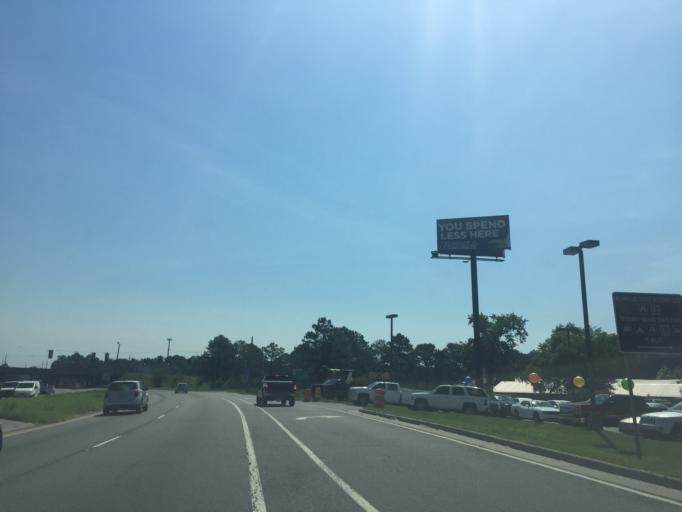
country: US
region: Georgia
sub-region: Chatham County
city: Georgetown
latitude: 31.9985
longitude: -81.2510
